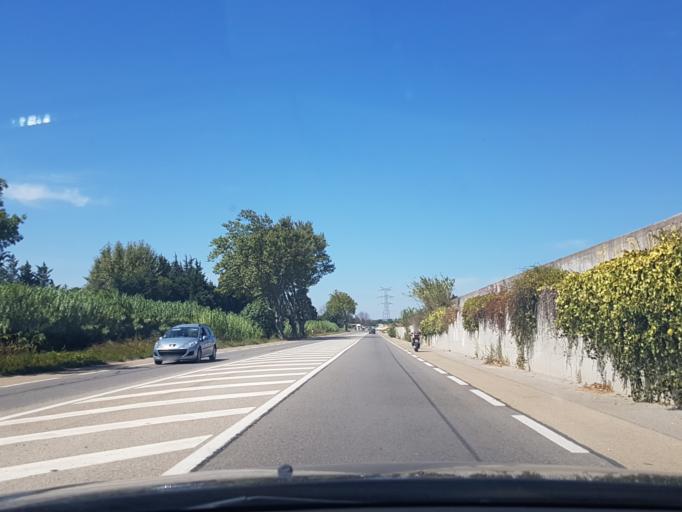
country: FR
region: Provence-Alpes-Cote d'Azur
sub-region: Departement des Bouches-du-Rhone
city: Rognonas
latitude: 43.9075
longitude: 4.8131
